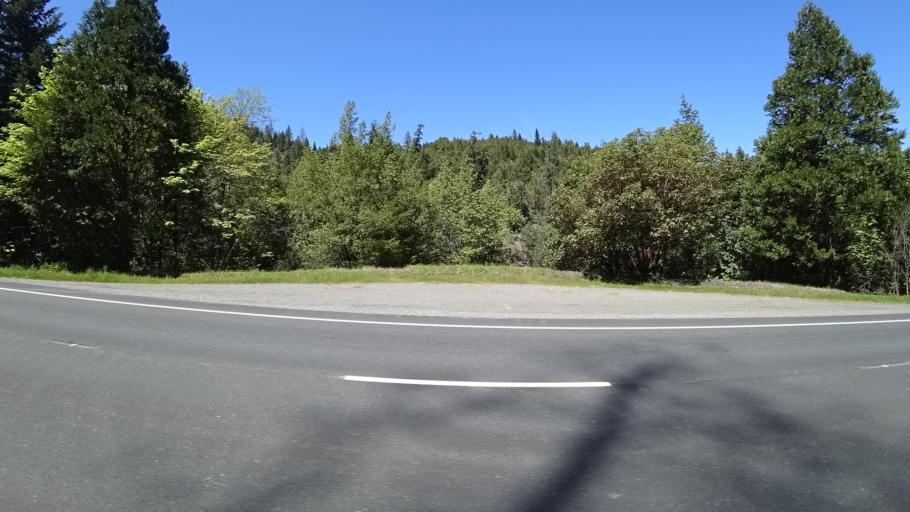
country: US
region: California
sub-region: Humboldt County
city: Willow Creek
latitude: 40.9419
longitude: -123.6676
